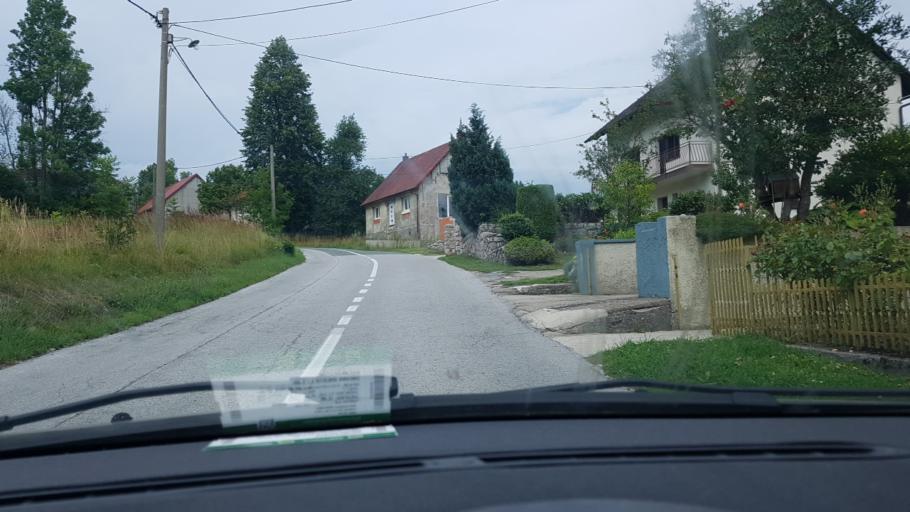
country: HR
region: Primorsko-Goranska
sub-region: Grad Delnice
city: Delnice
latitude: 45.3259
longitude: 14.7397
